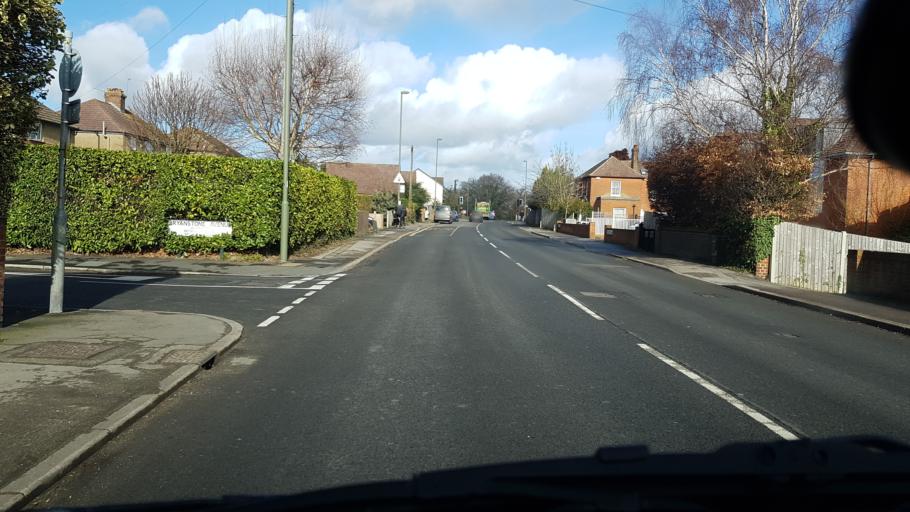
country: GB
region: England
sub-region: Surrey
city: Guildford
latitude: 51.2583
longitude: -0.5950
